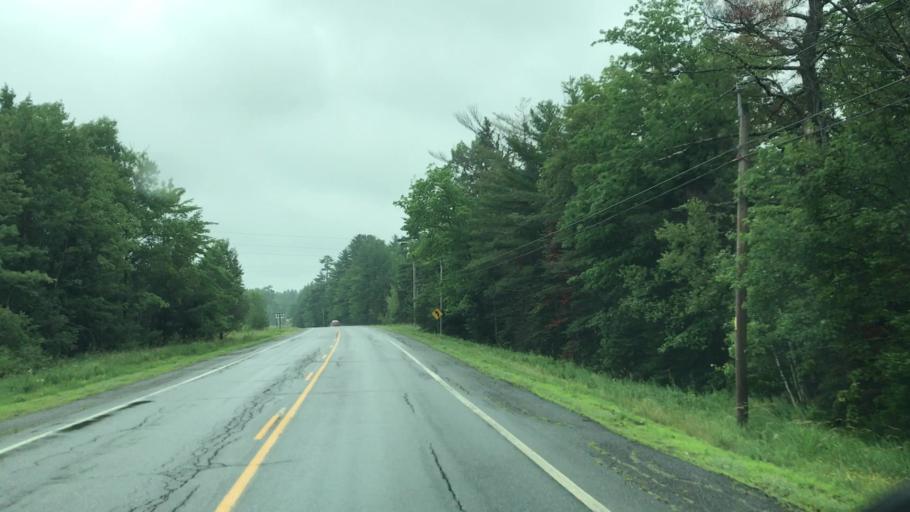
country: US
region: Maine
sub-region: Penobscot County
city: Howland
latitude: 45.2499
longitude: -68.6384
